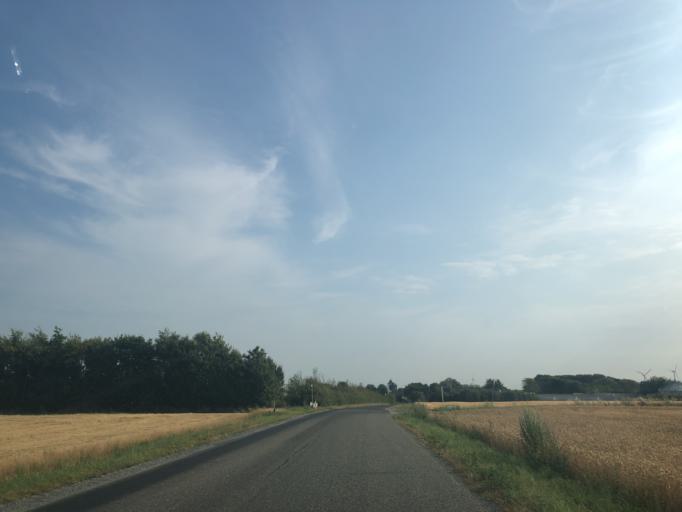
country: DK
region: Central Jutland
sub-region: Skive Kommune
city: Skive
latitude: 56.7249
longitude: 9.0235
